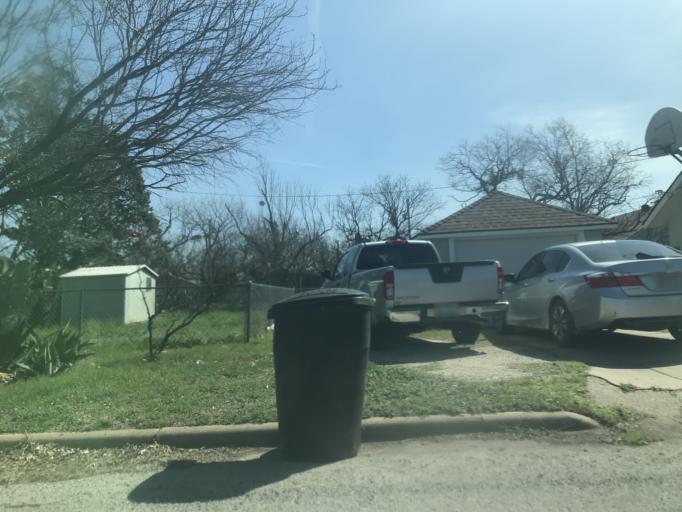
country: US
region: Texas
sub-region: Taylor County
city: Abilene
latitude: 32.4685
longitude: -99.7422
